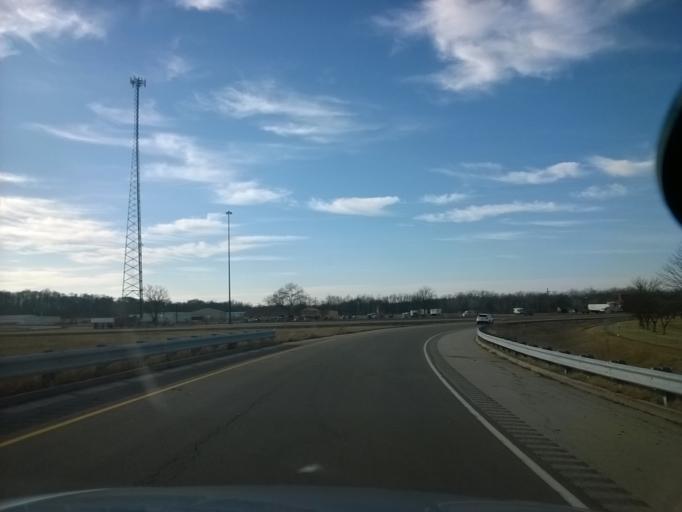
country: US
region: Indiana
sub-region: Johnson County
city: Edinburgh
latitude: 39.3070
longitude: -85.9612
